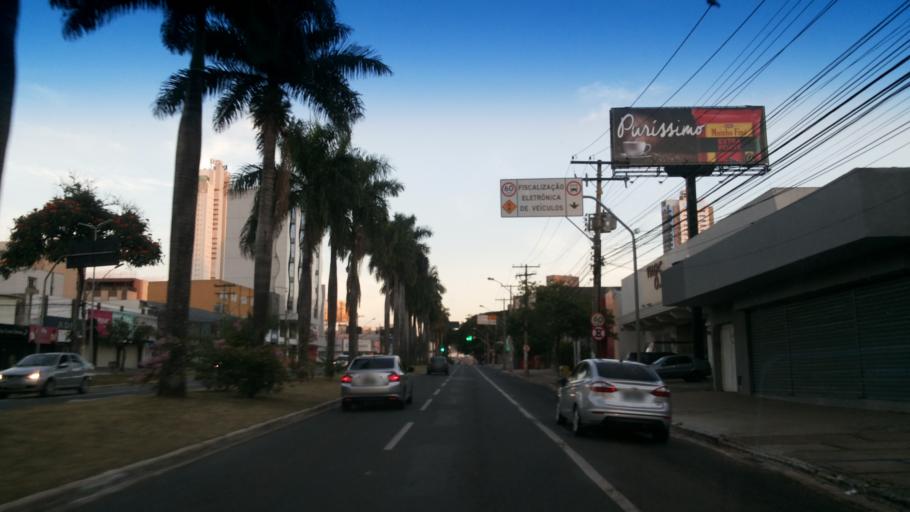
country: BR
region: Goias
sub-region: Goiania
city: Goiania
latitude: -16.7012
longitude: -49.2643
